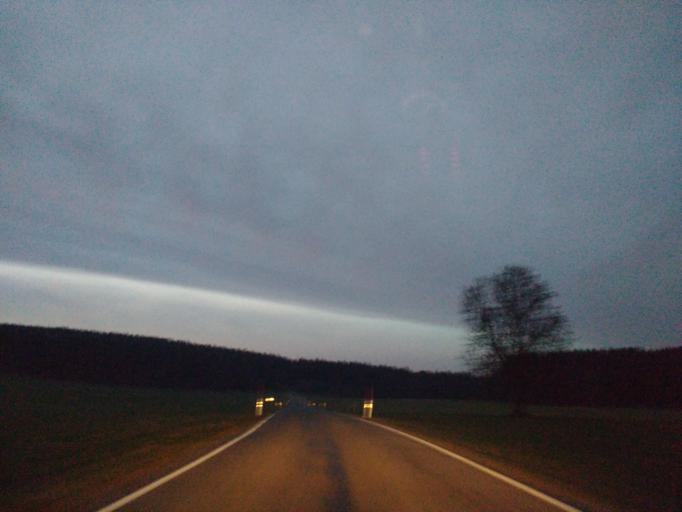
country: DE
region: Bavaria
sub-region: Swabia
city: Bidingen
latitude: 47.8425
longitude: 10.7126
